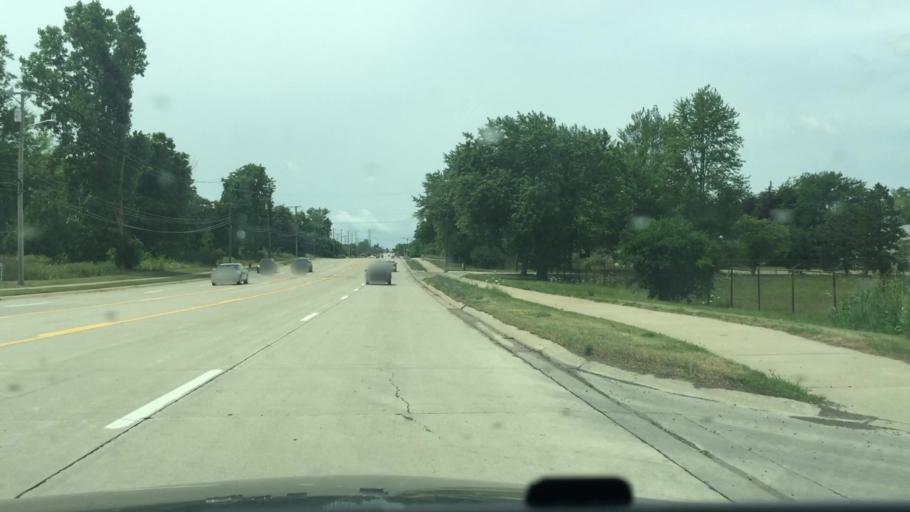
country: US
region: Michigan
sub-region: Oakland County
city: Novi
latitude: 42.4882
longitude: -83.5086
